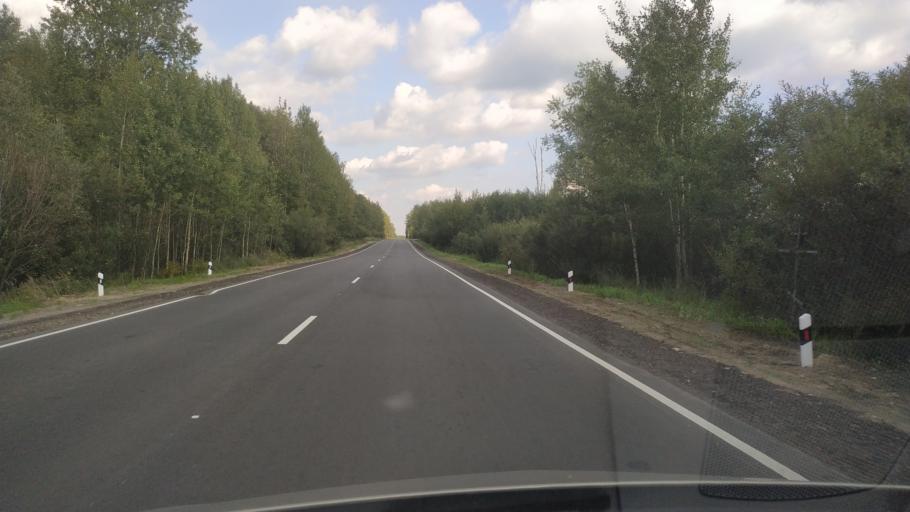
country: RU
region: Moskovskaya
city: Likino-Dulevo
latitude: 55.7277
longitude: 39.0277
